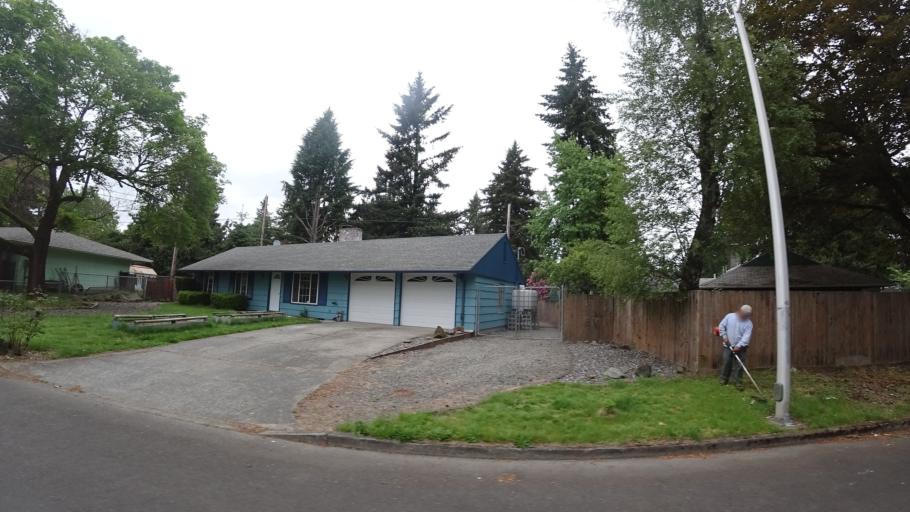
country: US
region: Oregon
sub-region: Multnomah County
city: Lents
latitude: 45.5117
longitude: -122.5170
